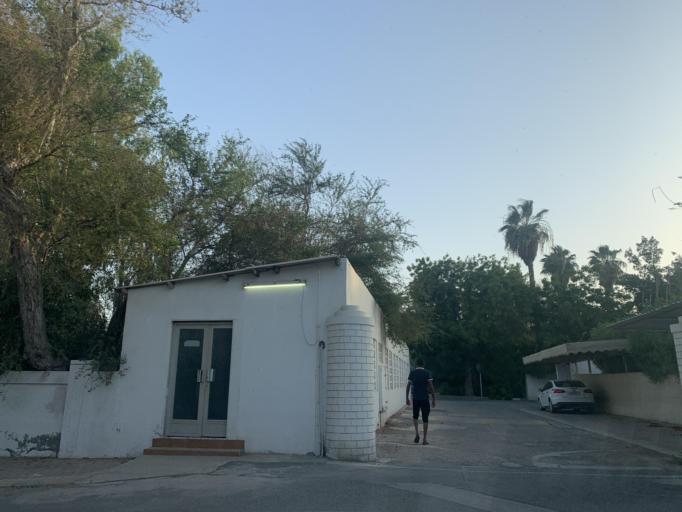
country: BH
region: Manama
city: Jidd Hafs
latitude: 26.2217
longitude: 50.5299
